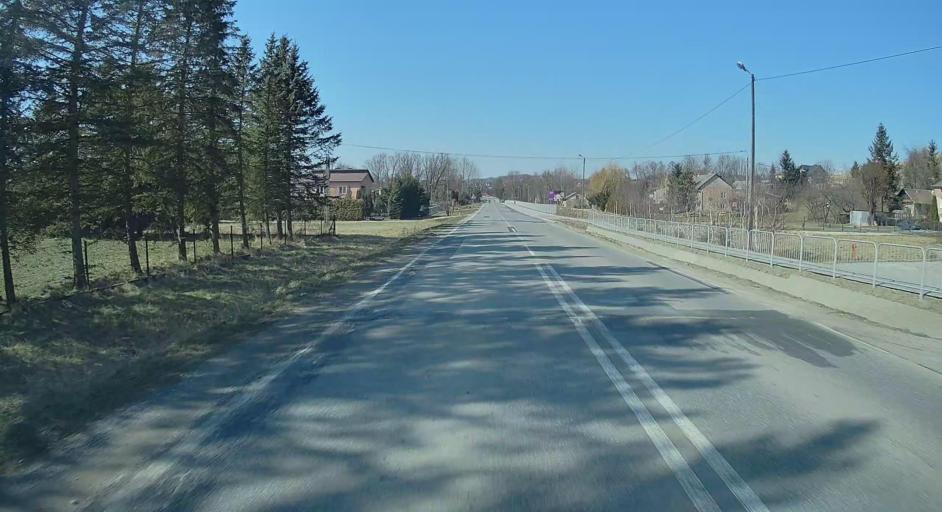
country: PL
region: Subcarpathian Voivodeship
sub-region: Powiat rzeszowski
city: Tyczyn
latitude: 49.9640
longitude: 22.0827
